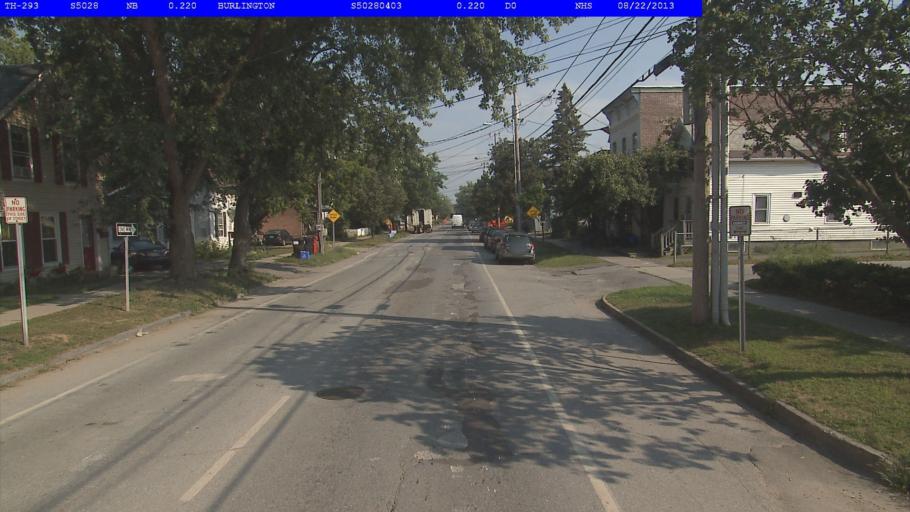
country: US
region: Vermont
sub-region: Chittenden County
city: Burlington
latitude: 44.4835
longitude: -73.2176
